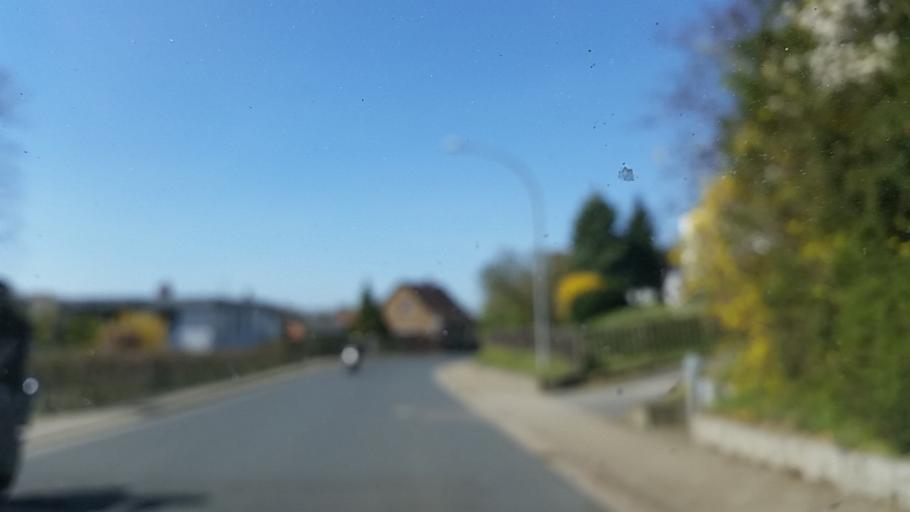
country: DE
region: Lower Saxony
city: Evessen
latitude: 52.2034
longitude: 10.7065
